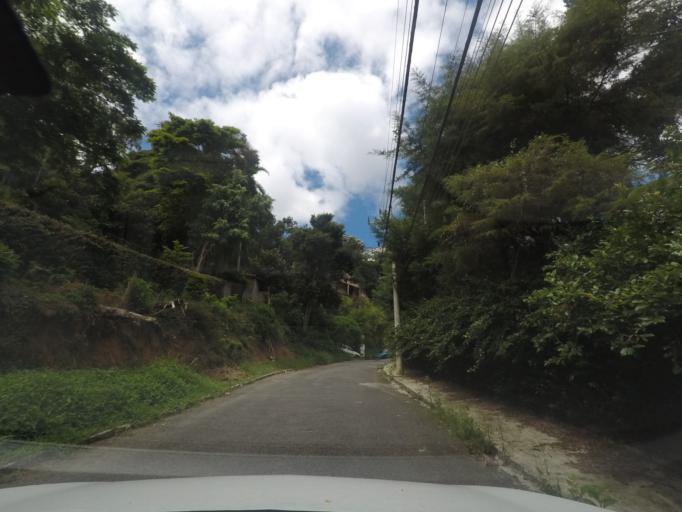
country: BR
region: Rio de Janeiro
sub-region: Teresopolis
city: Teresopolis
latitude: -22.4050
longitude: -42.9816
